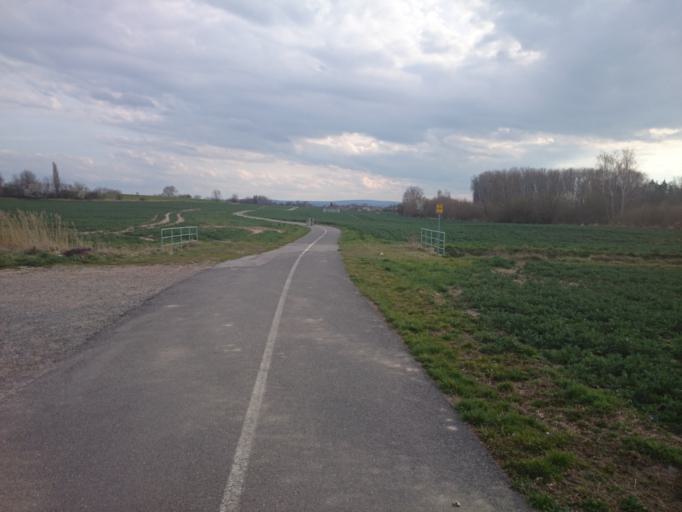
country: CZ
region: Pardubicky
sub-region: Okres Pardubice
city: Pardubice
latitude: 50.0111
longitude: 15.7636
